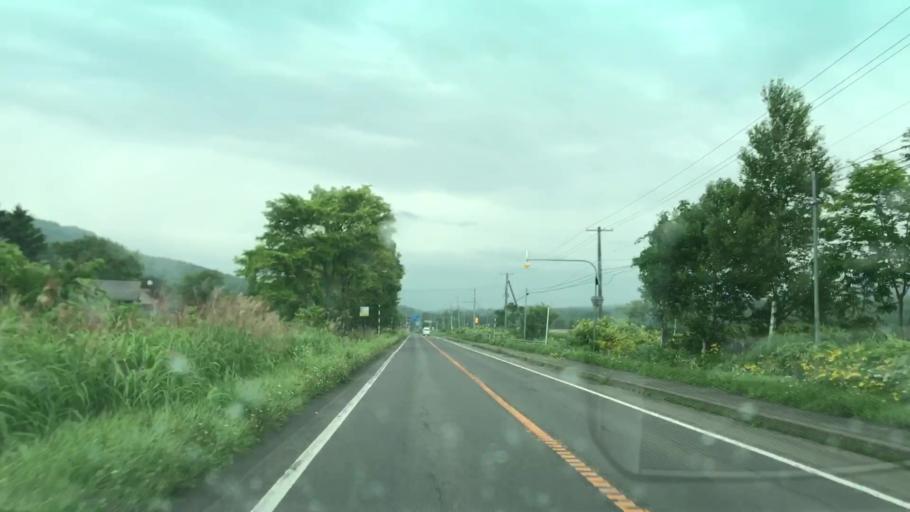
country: JP
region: Hokkaido
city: Niseko Town
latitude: 42.7667
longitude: 140.4839
